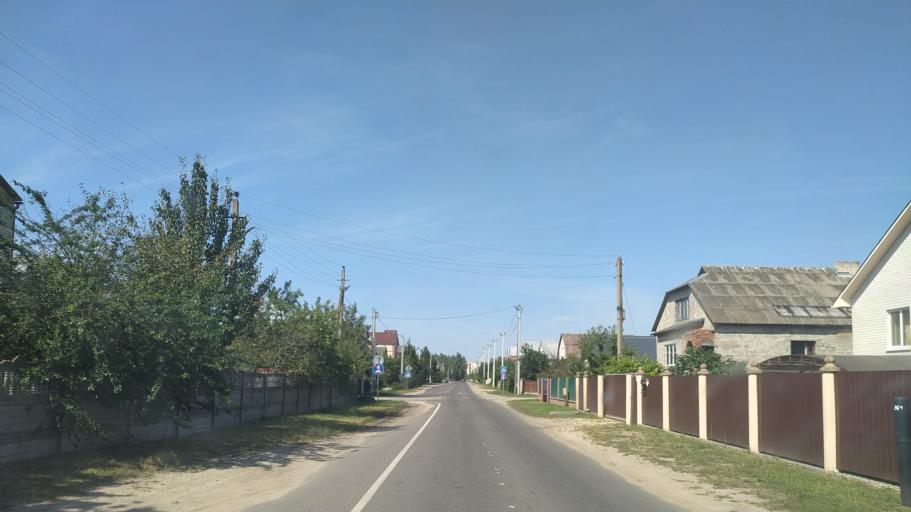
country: BY
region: Brest
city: Byaroza
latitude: 52.5307
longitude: 24.9956
